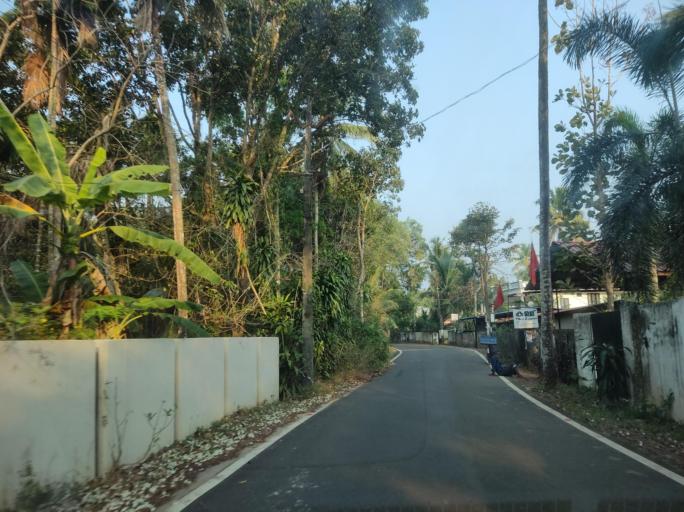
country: IN
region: Kerala
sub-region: Alappuzha
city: Shertallai
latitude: 9.6155
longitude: 76.3134
